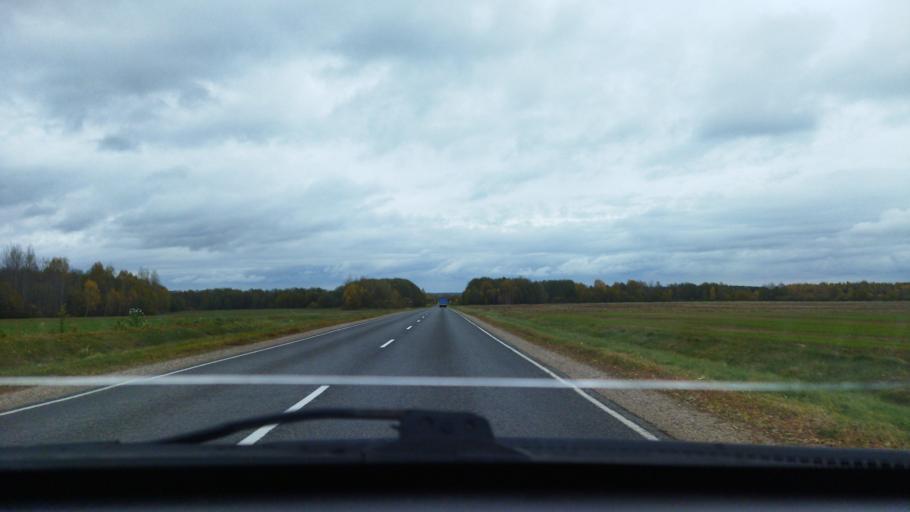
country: BY
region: Grodnenskaya
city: Astravyets
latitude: 54.7992
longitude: 26.1175
